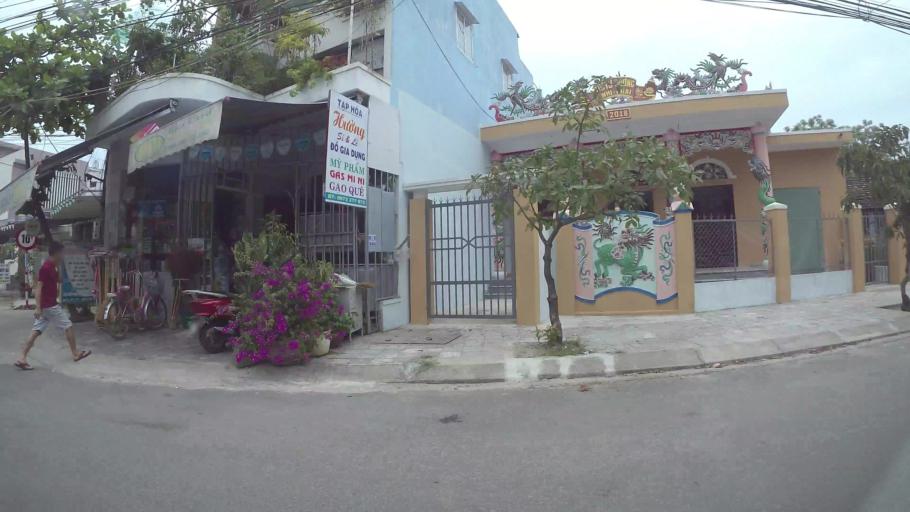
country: VN
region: Da Nang
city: Lien Chieu
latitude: 16.0720
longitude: 108.1665
